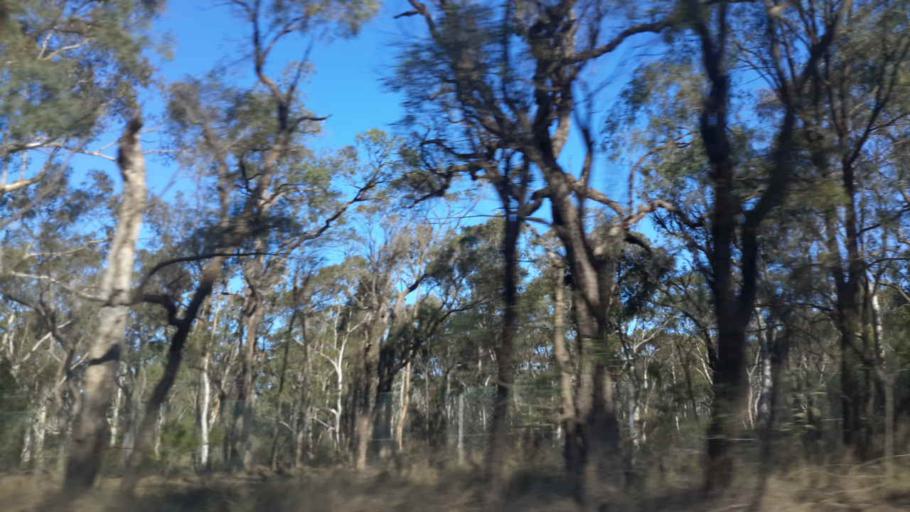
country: AU
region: New South Wales
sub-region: Hawkesbury
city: South Windsor
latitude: -33.6546
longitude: 150.7721
